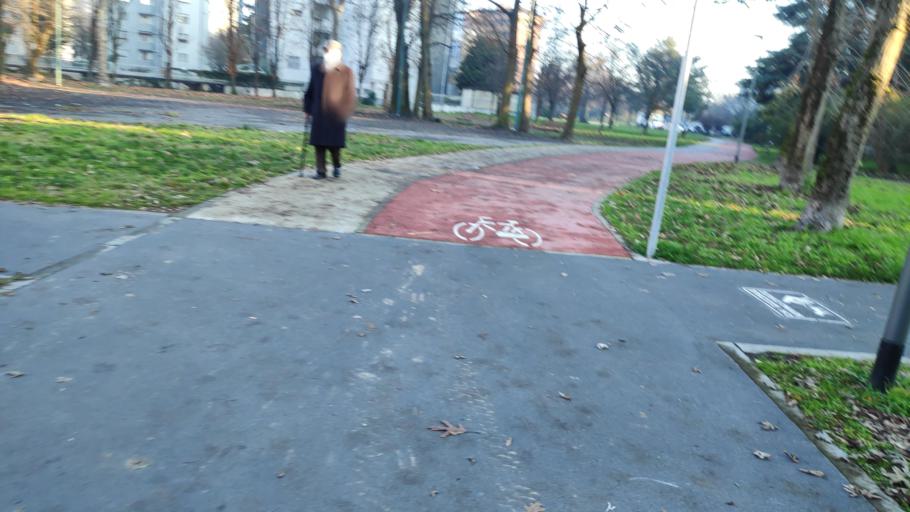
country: IT
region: Lombardy
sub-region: Citta metropolitana di Milano
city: Cologno Monzese
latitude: 45.5301
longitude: 9.2814
